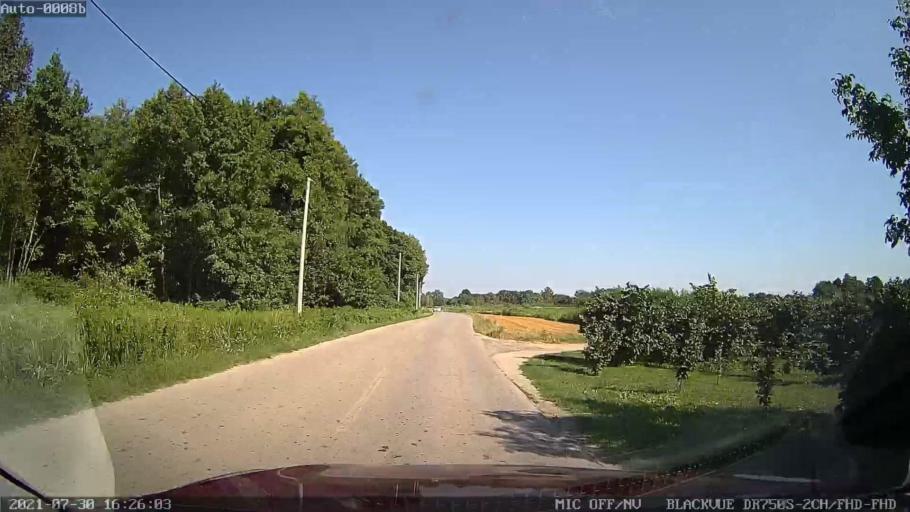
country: HR
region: Medimurska
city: Kursanec
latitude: 46.2800
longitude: 16.4183
